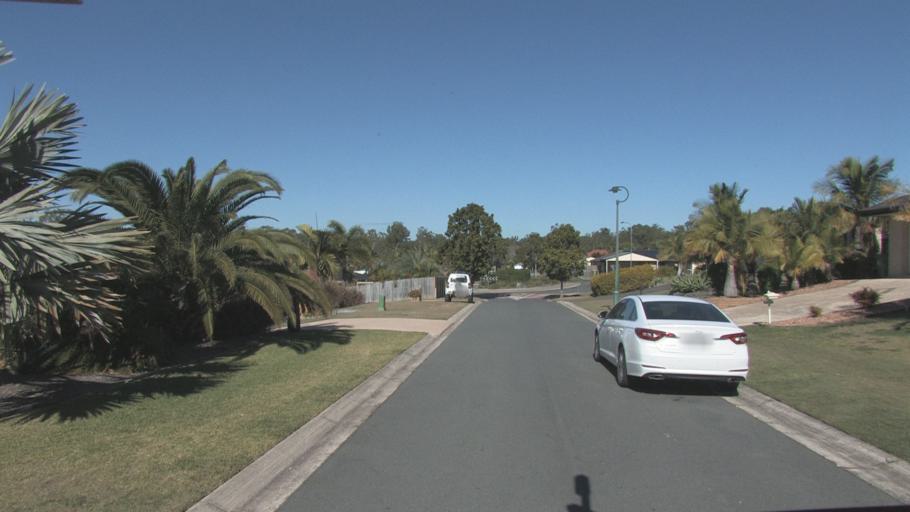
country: AU
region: Queensland
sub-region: Logan
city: Logan Reserve
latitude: -27.6894
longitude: 153.0625
